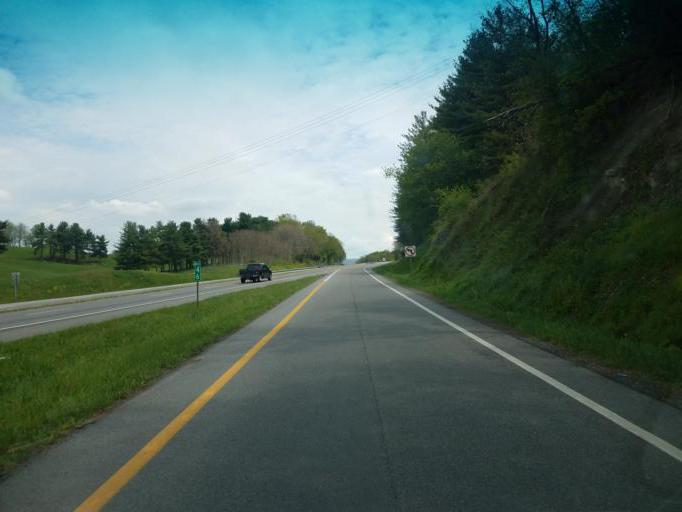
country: US
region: Virginia
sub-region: Smyth County
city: Marion
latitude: 36.8287
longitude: -81.5041
